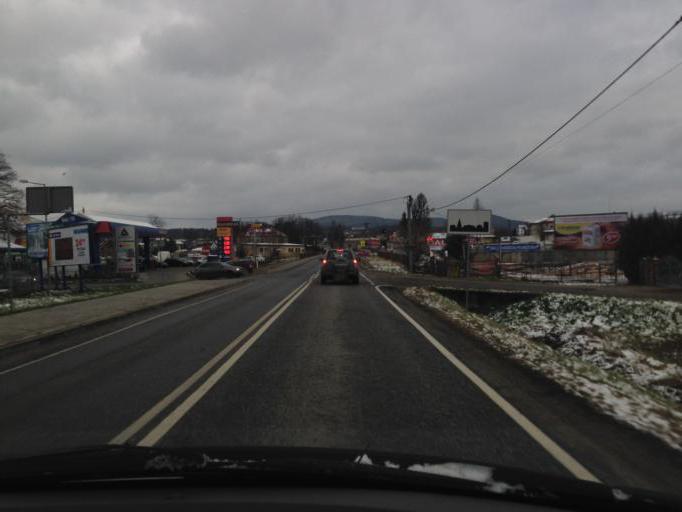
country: PL
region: Lesser Poland Voivodeship
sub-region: Powiat tarnowski
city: Zakliczyn
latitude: 49.8595
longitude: 20.8139
